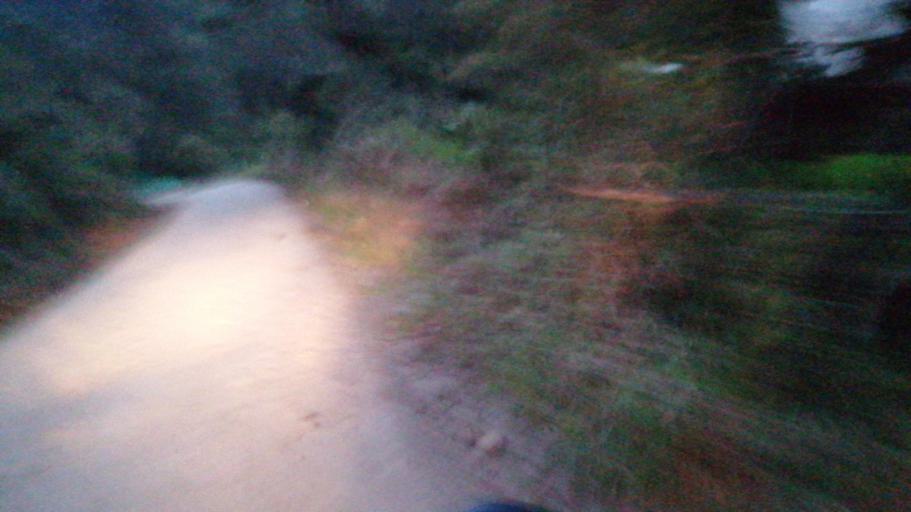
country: CO
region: Boyaca
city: Chinavita
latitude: 5.1447
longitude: -73.3995
